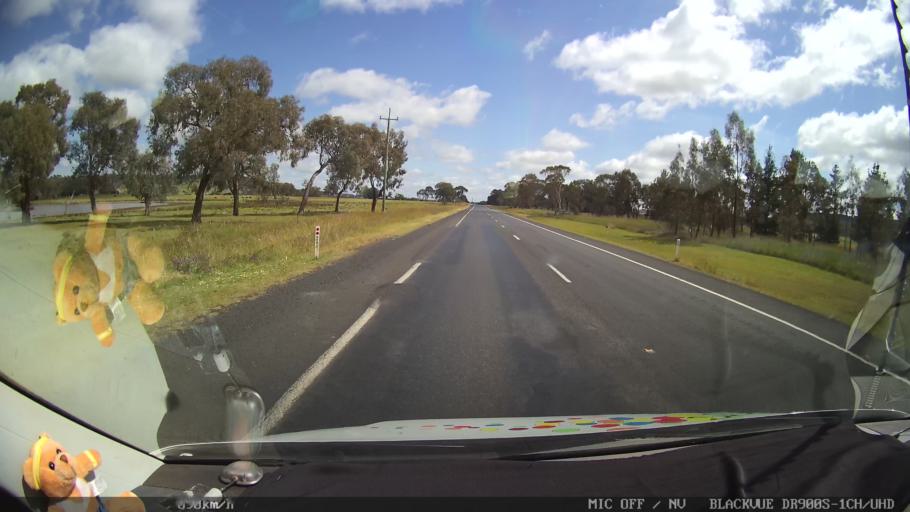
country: AU
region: New South Wales
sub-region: Glen Innes Severn
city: Glen Innes
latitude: -29.8740
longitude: 151.7349
